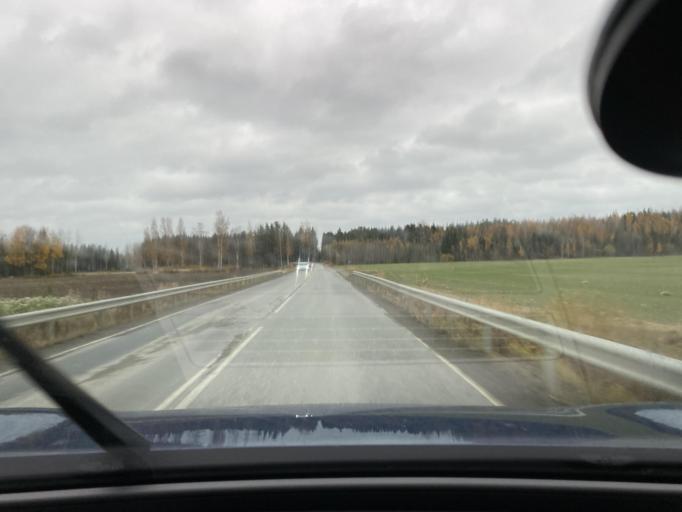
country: FI
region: Satakunta
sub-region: Pori
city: Huittinen
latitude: 61.1275
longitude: 22.5954
